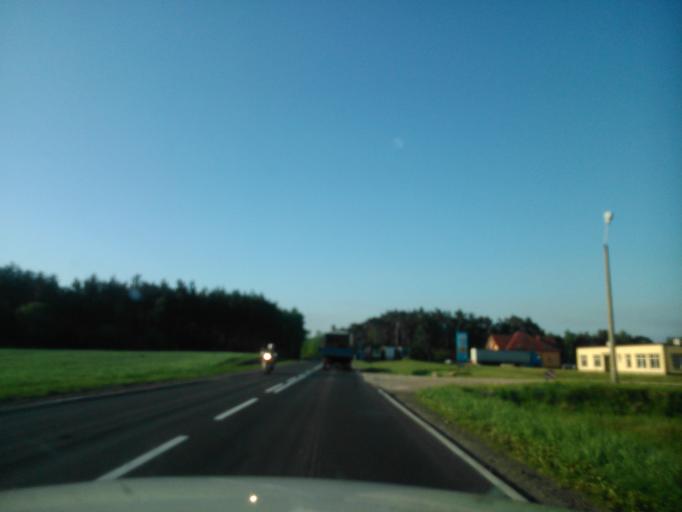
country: PL
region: Masovian Voivodeship
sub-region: Powiat plocki
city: Wyszogrod
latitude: 52.3498
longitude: 20.2097
